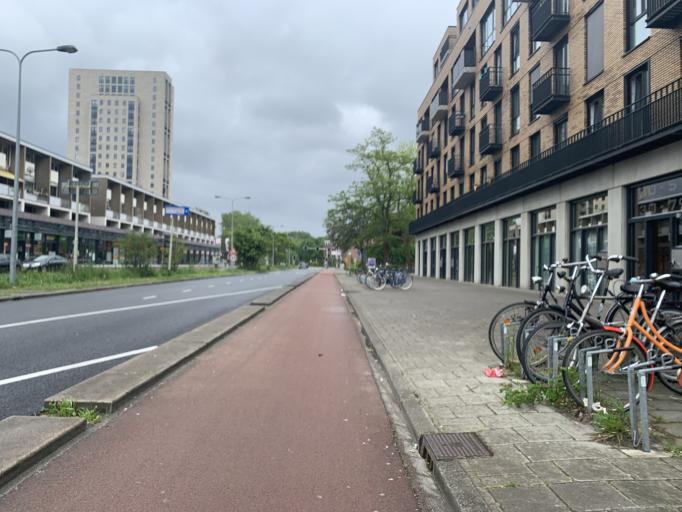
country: NL
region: Groningen
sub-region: Gemeente Groningen
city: Korrewegwijk
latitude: 53.2301
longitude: 6.5420
